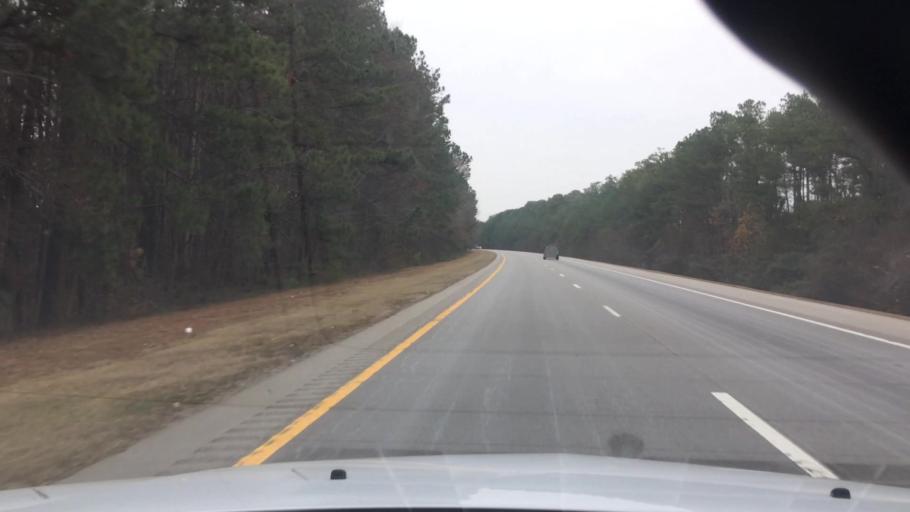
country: US
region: North Carolina
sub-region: Wilson County
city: Wilson
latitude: 35.7932
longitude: -77.9924
